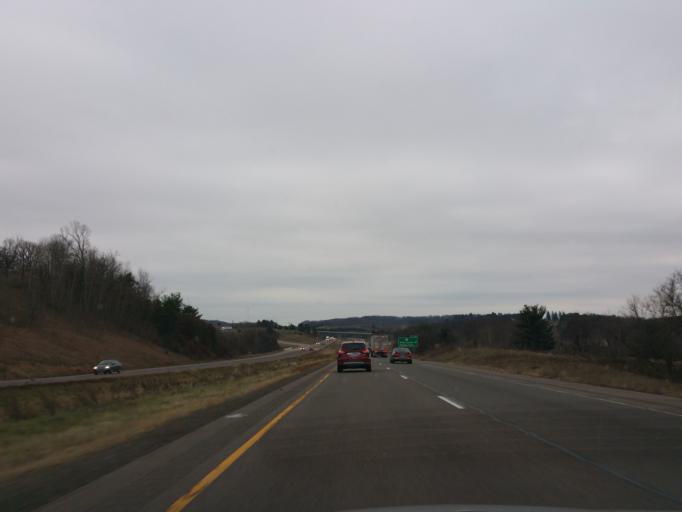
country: US
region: Wisconsin
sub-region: Trempealeau County
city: Osseo
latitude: 44.4654
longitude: -91.0979
